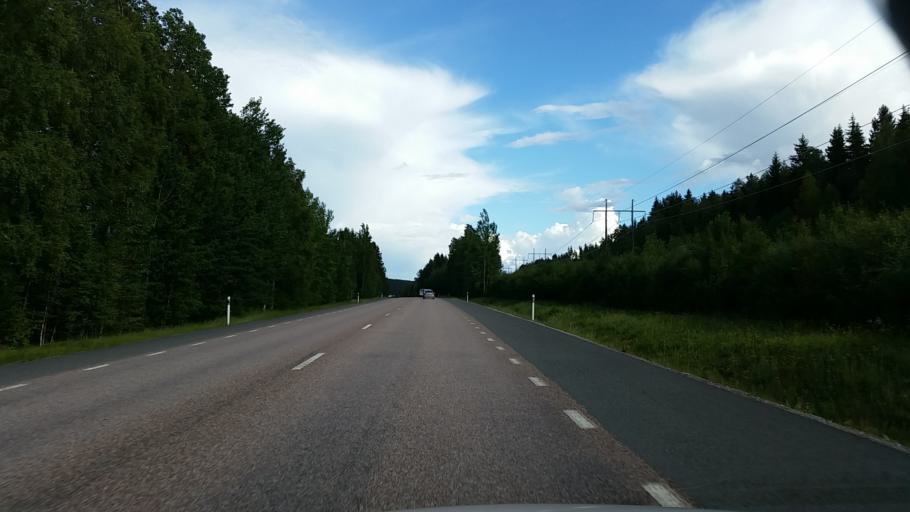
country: SE
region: Vaestmanland
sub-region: Fagersta Kommun
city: Fagersta
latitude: 60.0123
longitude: 15.6396
